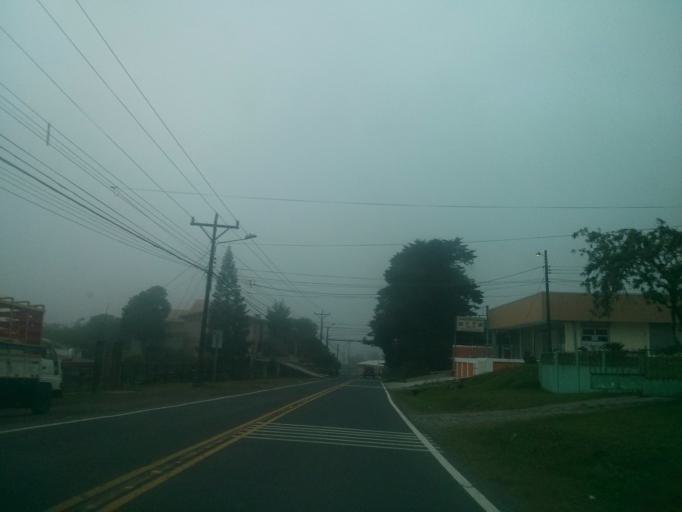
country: CR
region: Cartago
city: Cot
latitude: 9.8903
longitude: -83.8414
